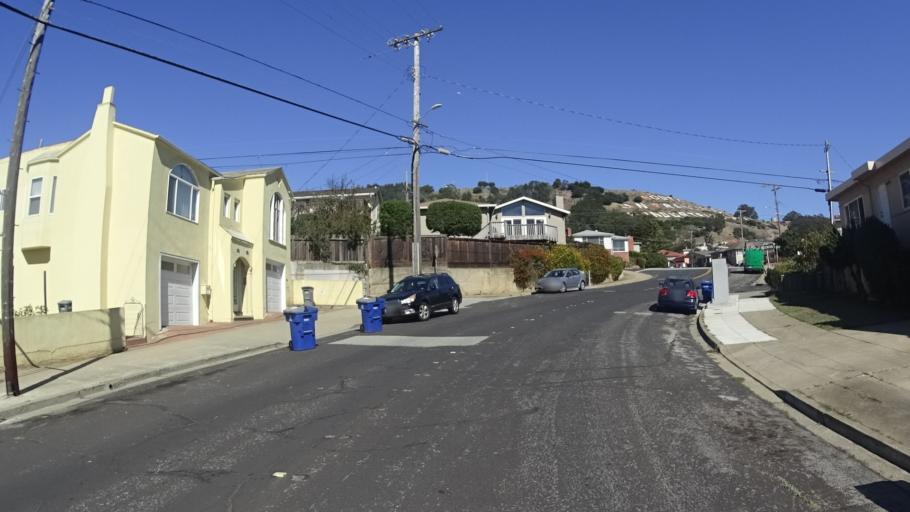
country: US
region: California
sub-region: San Mateo County
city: South San Francisco
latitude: 37.6592
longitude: -122.4226
